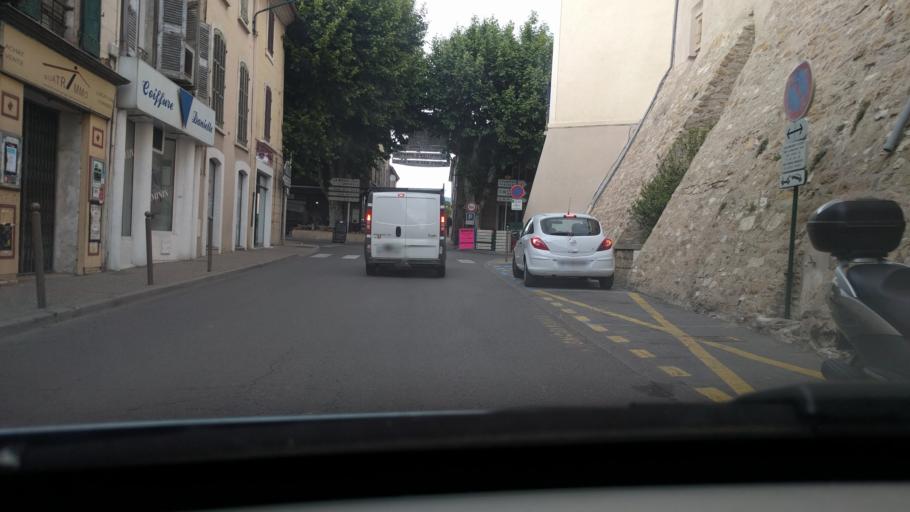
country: FR
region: Provence-Alpes-Cote d'Azur
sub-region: Departement du Vaucluse
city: Grambois
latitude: 43.7256
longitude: 5.5479
